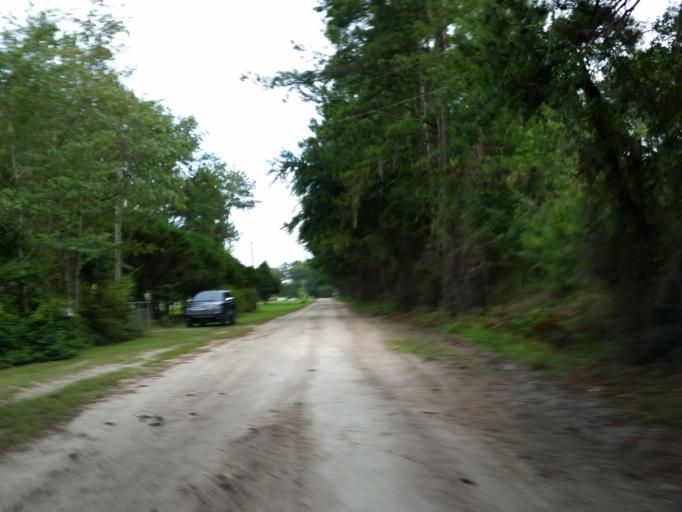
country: US
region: Florida
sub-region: Alachua County
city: High Springs
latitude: 29.9534
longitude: -82.5594
